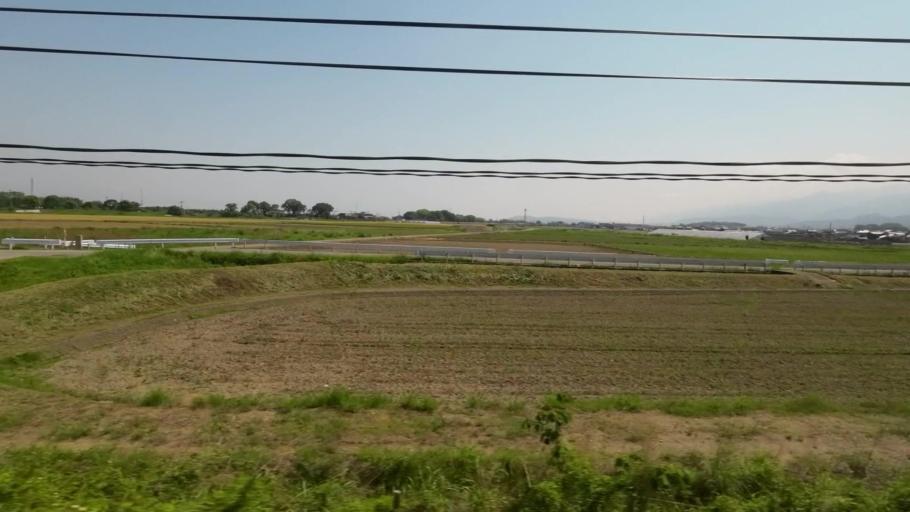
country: JP
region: Ehime
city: Saijo
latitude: 33.9013
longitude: 133.1001
